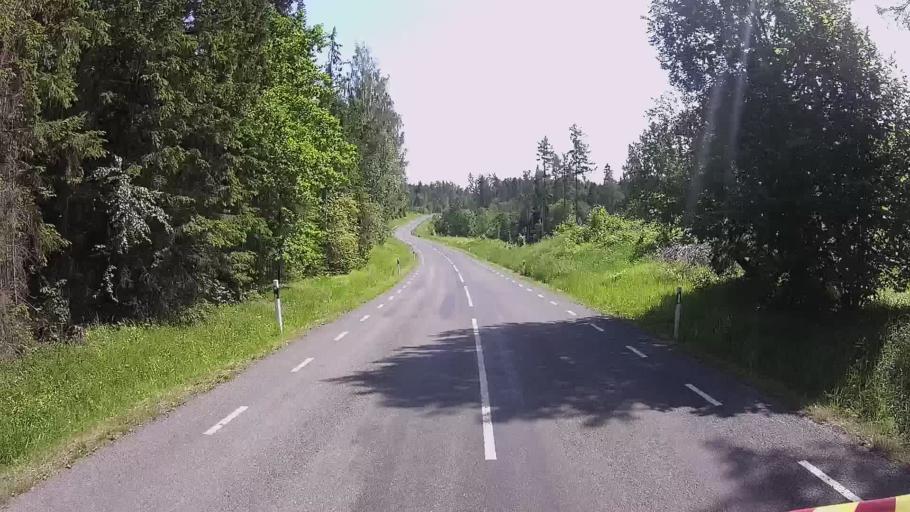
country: EE
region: Viljandimaa
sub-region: Karksi vald
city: Karksi-Nuia
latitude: 58.0841
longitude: 25.5574
